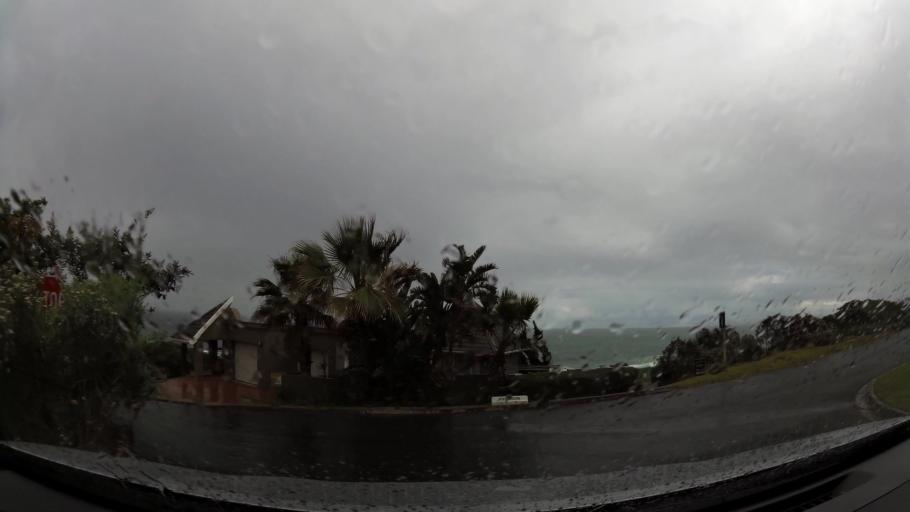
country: ZA
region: Western Cape
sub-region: Eden District Municipality
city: Mossel Bay
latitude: -34.0543
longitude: 22.2477
